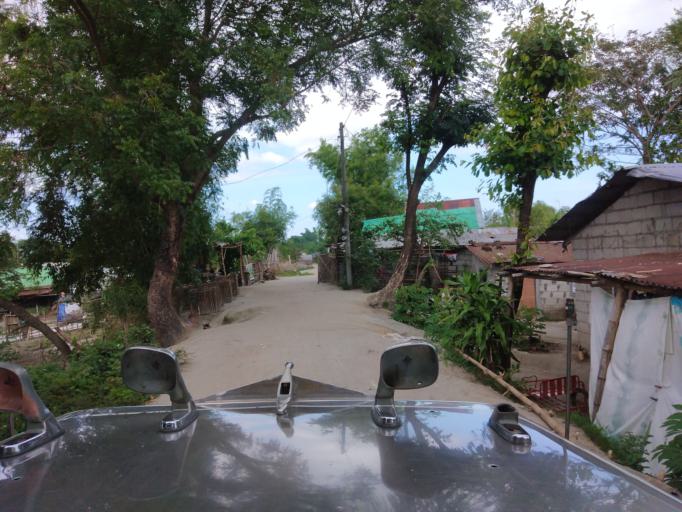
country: PH
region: Central Luzon
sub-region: Province of Pampanga
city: San Patricio
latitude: 15.1155
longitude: 120.7100
